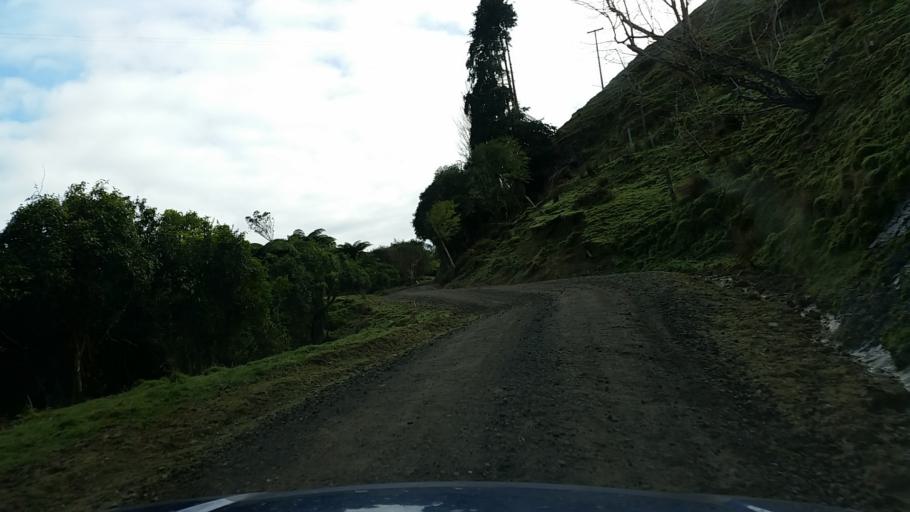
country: NZ
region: Taranaki
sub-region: New Plymouth District
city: Waitara
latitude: -39.1077
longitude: 174.8479
